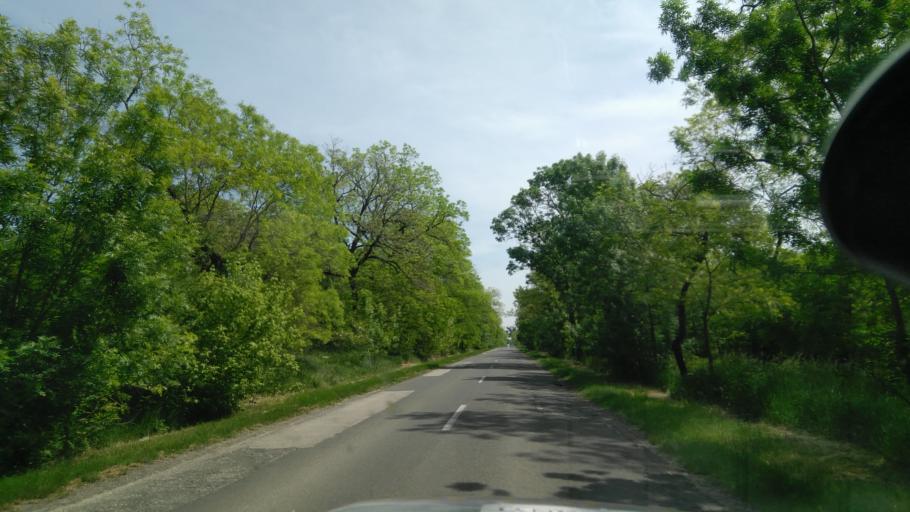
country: HU
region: Csongrad
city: Fabiansebestyen
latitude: 46.5756
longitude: 20.4531
